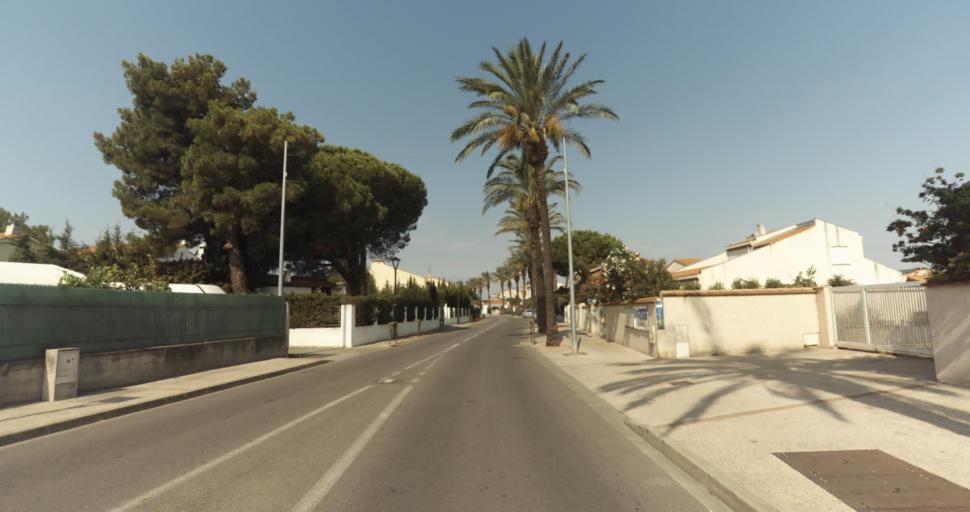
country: FR
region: Languedoc-Roussillon
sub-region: Departement des Pyrenees-Orientales
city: Latour-Bas-Elne
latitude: 42.6190
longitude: 3.0092
